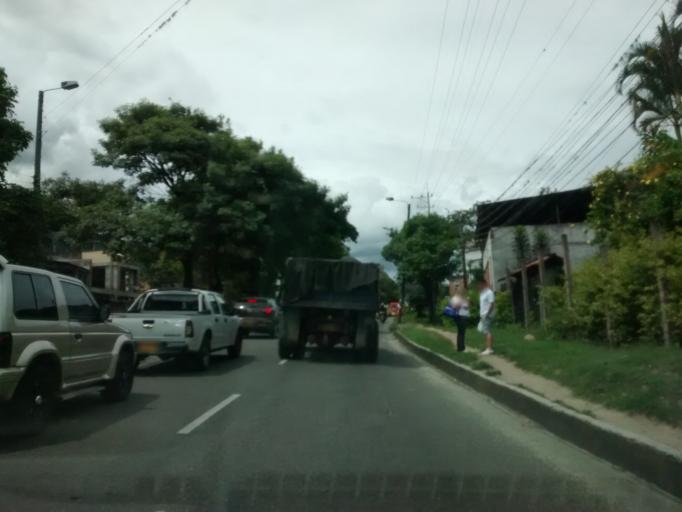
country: CO
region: Tolima
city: Ibague
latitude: 4.4473
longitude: -75.2028
